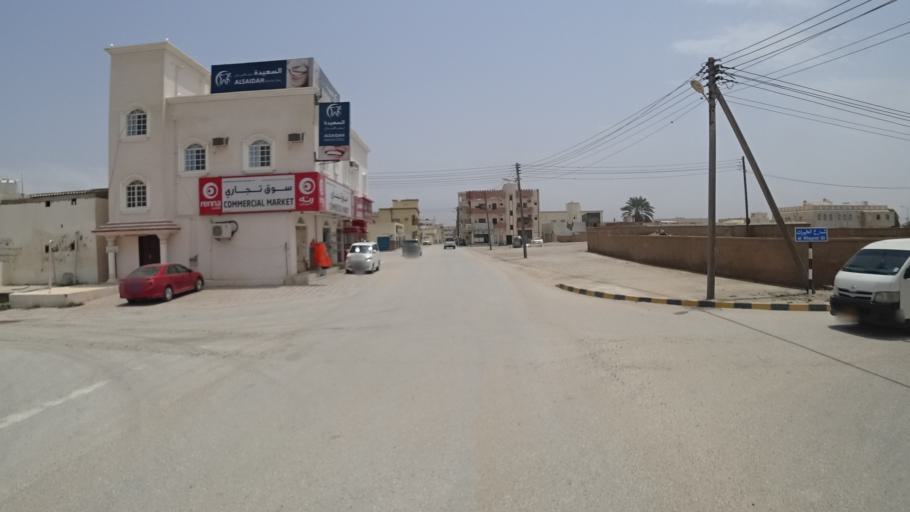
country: OM
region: Zufar
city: Salalah
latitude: 16.9837
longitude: 54.6925
